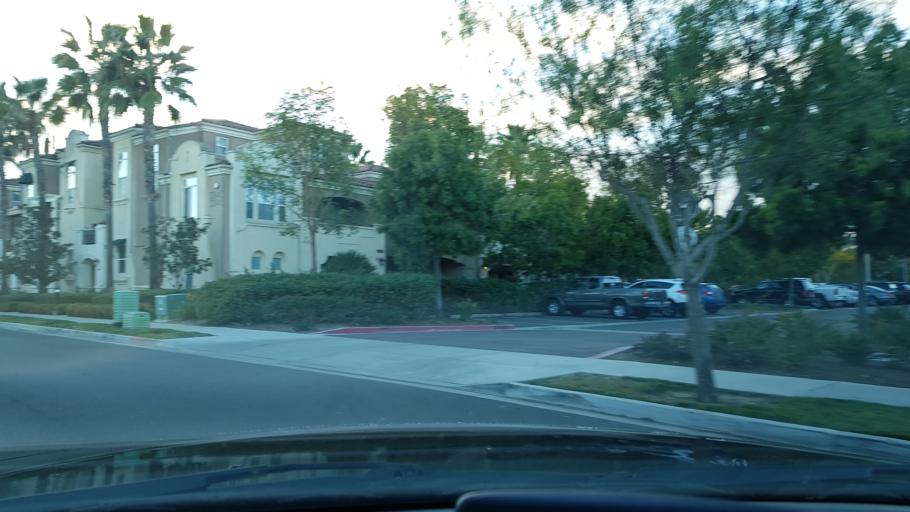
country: US
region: California
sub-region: San Diego County
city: Coronado
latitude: 32.7332
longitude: -117.2160
